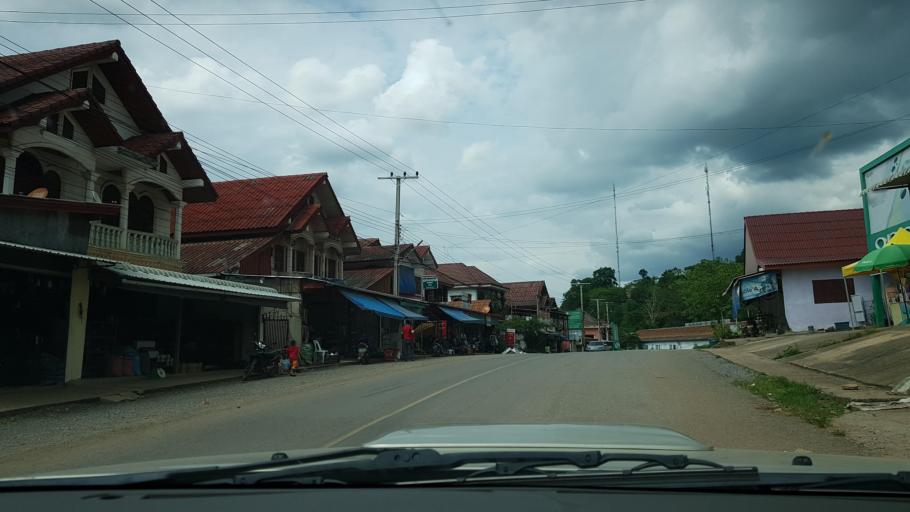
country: LA
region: Loungnamtha
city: Muang Nale
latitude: 20.2986
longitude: 101.6370
